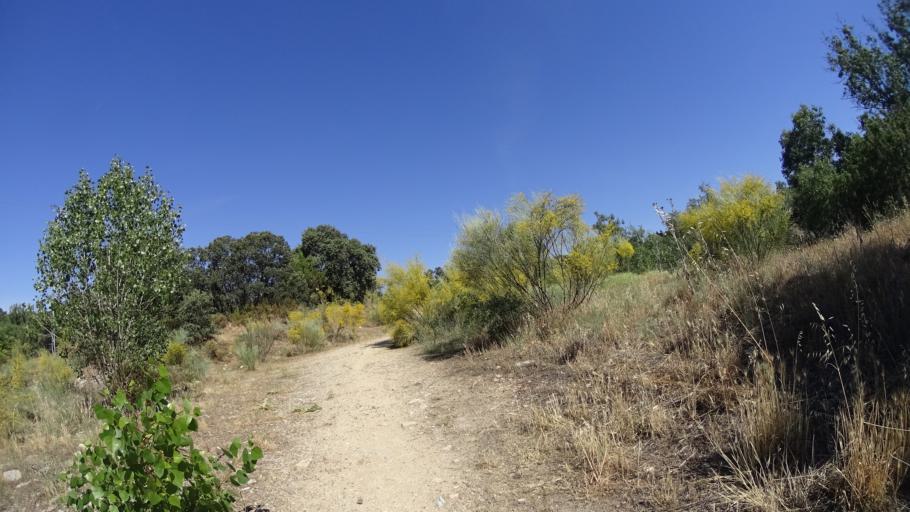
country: ES
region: Madrid
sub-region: Provincia de Madrid
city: Galapagar
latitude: 40.5867
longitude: -3.9670
